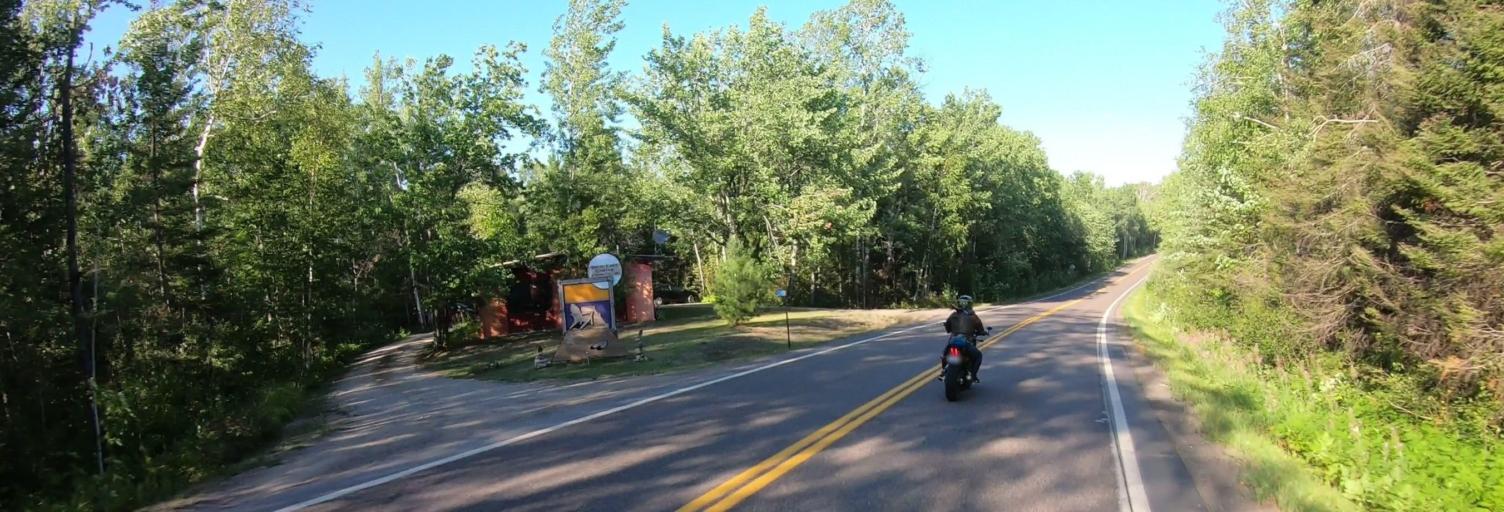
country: US
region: Minnesota
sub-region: Saint Louis County
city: Ely
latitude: 47.9618
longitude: -91.5663
